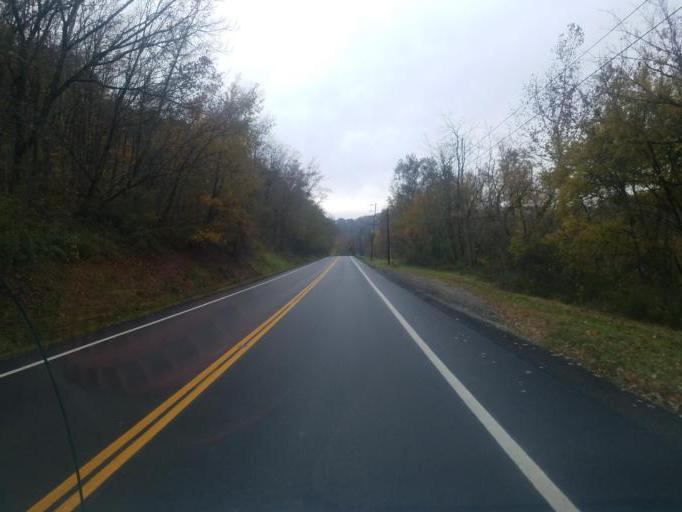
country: US
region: Ohio
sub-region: Washington County
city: Devola
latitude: 39.5383
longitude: -81.5459
